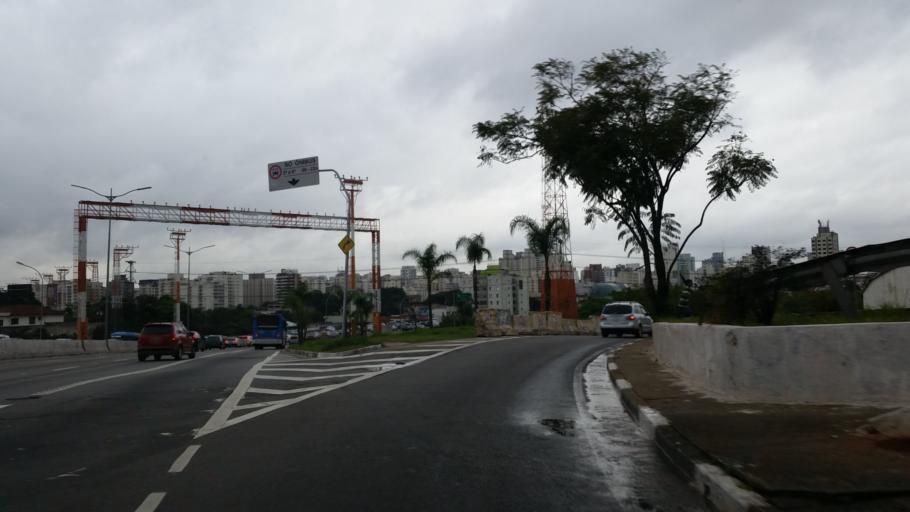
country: BR
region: Sao Paulo
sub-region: Sao Paulo
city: Sao Paulo
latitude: -23.6196
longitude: -46.6619
